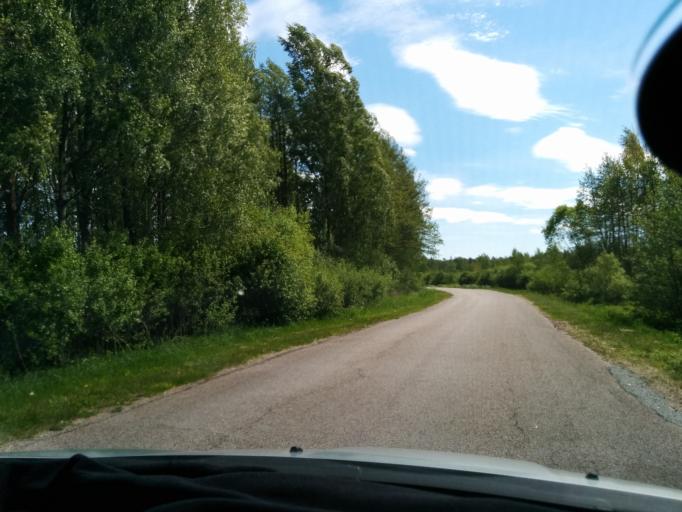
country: EE
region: Harju
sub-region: Loksa linn
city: Loksa
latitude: 59.5831
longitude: 25.9108
